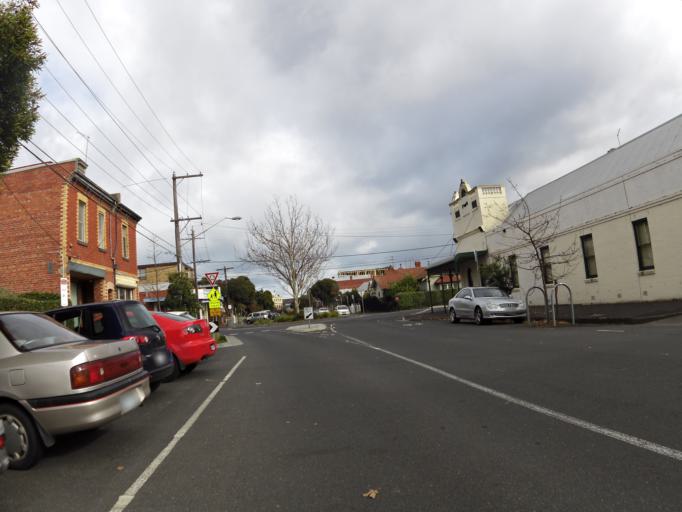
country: AU
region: Victoria
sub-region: Yarra
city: Clifton Hill
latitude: -37.7877
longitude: 145.0007
